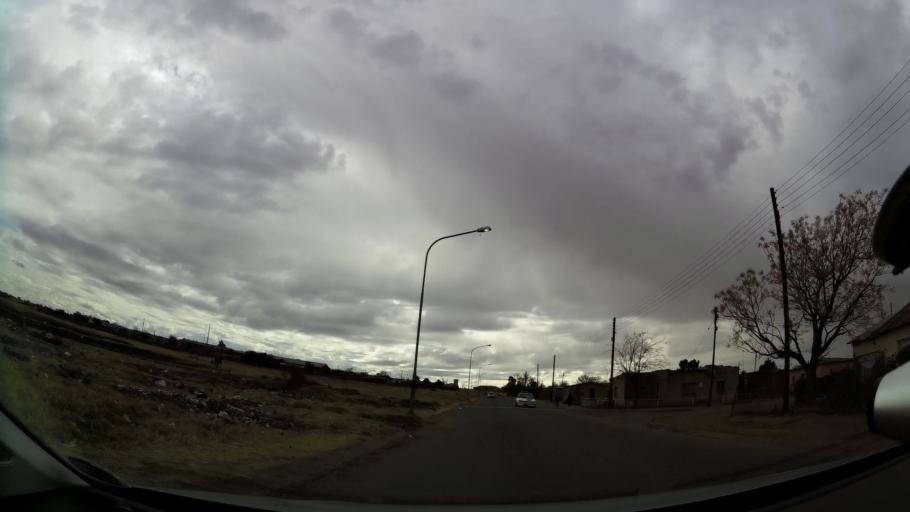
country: ZA
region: Orange Free State
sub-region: Fezile Dabi District Municipality
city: Kroonstad
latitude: -27.6561
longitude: 27.2018
